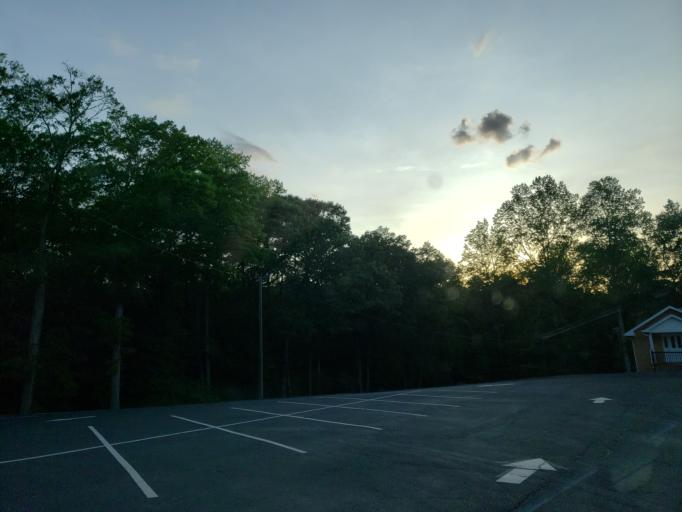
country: US
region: Georgia
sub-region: Coweta County
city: Newnan
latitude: 33.4899
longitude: -84.9145
